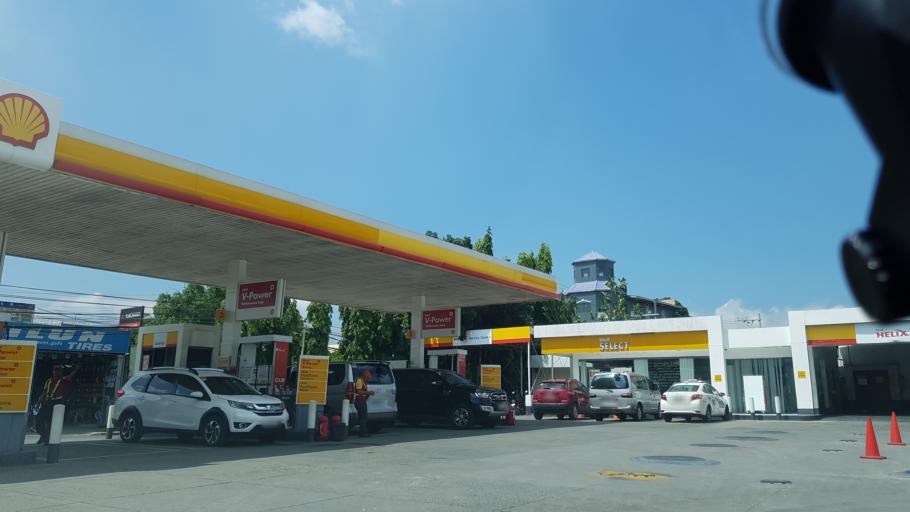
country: PH
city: Sambayanihan People's Village
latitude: 14.4621
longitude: 120.9916
